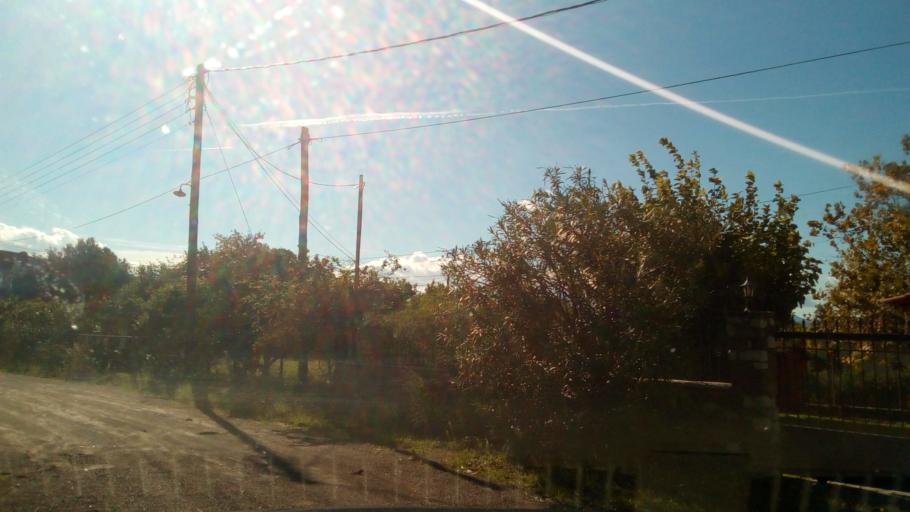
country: GR
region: West Greece
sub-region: Nomos Achaias
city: Kamarai
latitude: 38.3953
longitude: 22.0006
